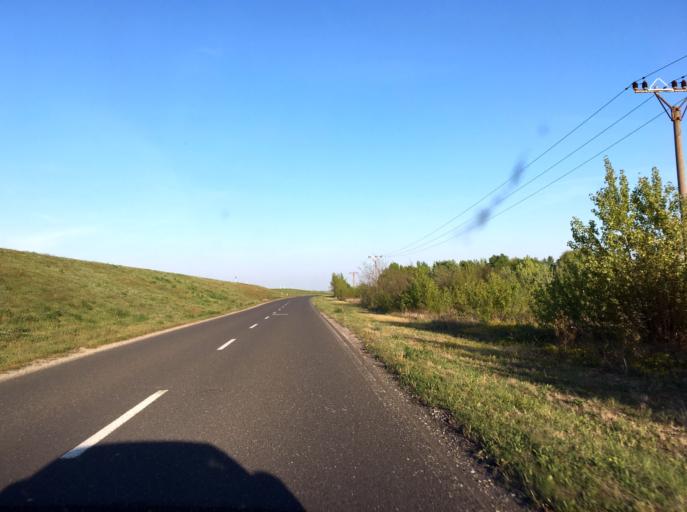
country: SK
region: Trnavsky
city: Samorin
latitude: 47.9966
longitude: 17.3306
